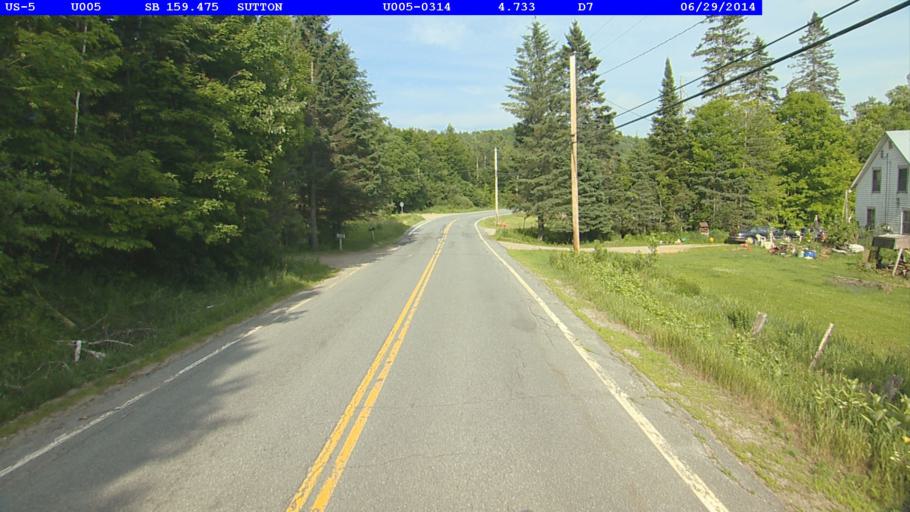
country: US
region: Vermont
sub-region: Caledonia County
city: Lyndonville
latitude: 44.6881
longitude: -72.0474
